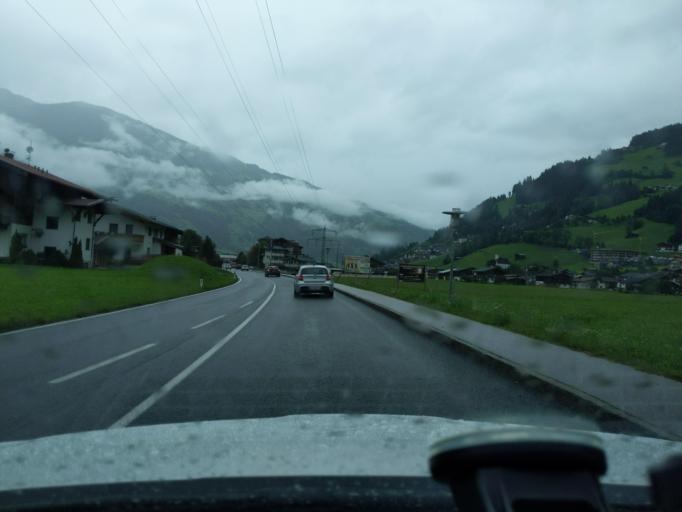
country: AT
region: Tyrol
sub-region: Politischer Bezirk Schwaz
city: Ramsau im Zillertal
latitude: 47.1988
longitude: 11.8721
